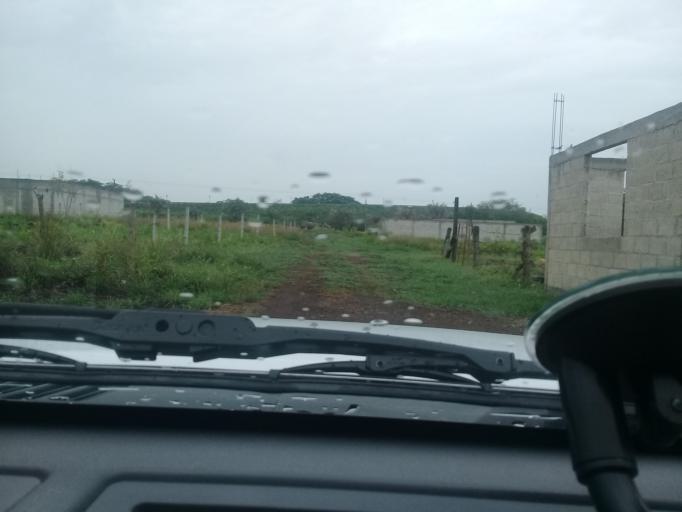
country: MX
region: Veracruz
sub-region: Puente Nacional
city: Cabezas
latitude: 19.3664
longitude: -96.3881
